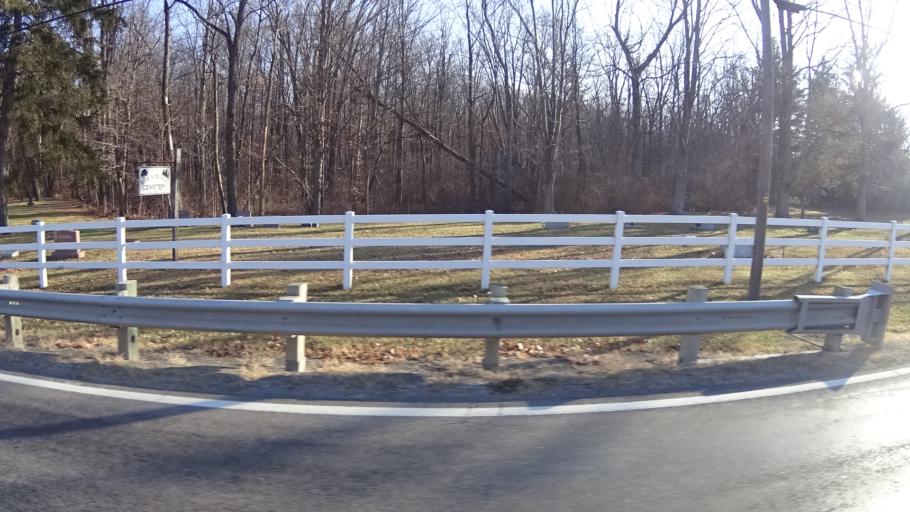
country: US
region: Ohio
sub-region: Lorain County
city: Lagrange
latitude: 41.2658
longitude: -82.1575
